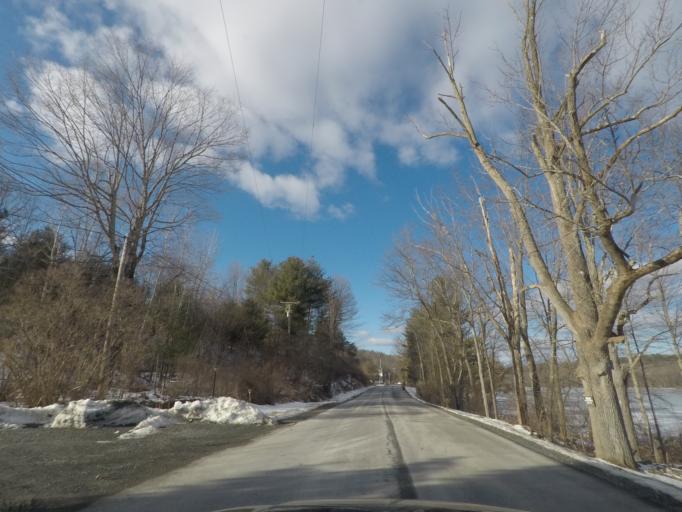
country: US
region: New York
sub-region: Rensselaer County
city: Nassau
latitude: 42.5280
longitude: -73.5287
